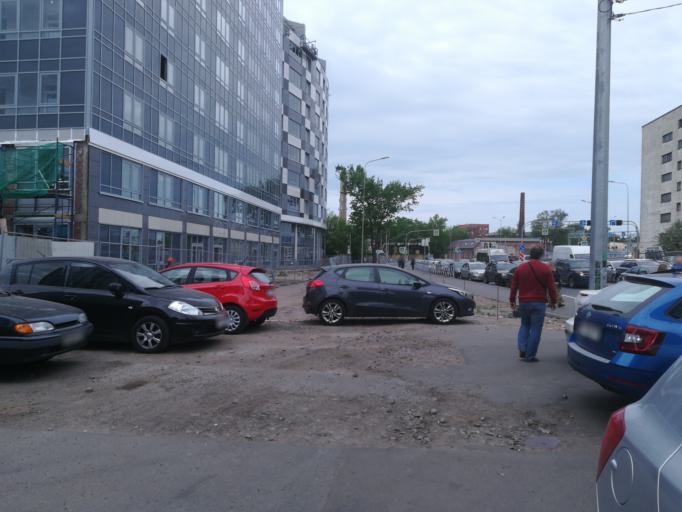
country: RU
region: St.-Petersburg
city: Vasyl'evsky Ostrov
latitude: 59.9509
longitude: 30.2661
